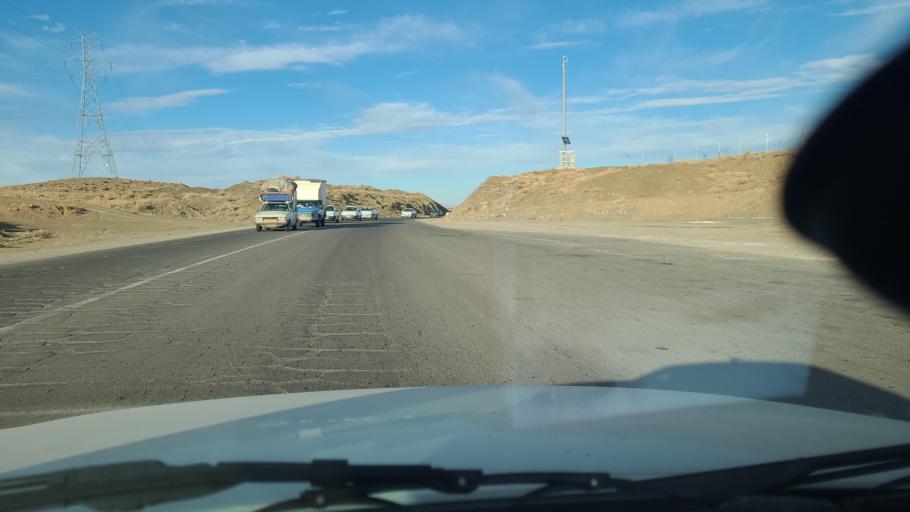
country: IR
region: Razavi Khorasan
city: Sabzevar
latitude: 36.4090
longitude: 57.5485
